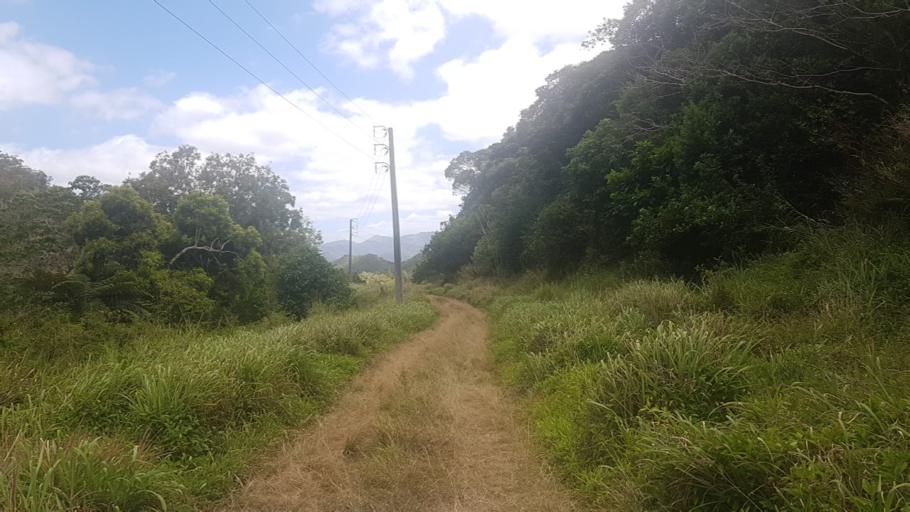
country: NC
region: South Province
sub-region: Dumbea
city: Dumbea
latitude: -22.1868
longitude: 166.4797
